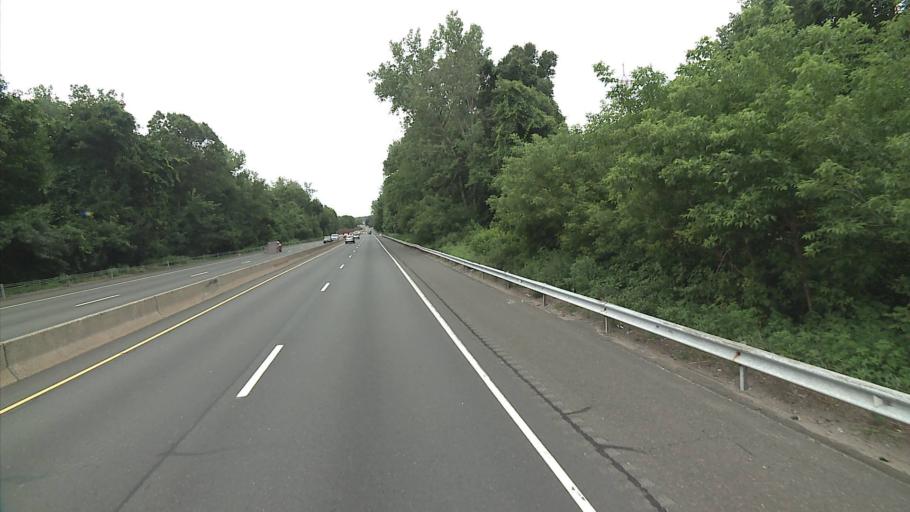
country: US
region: Connecticut
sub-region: New Haven County
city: Ansonia
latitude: 41.3479
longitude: -73.0945
